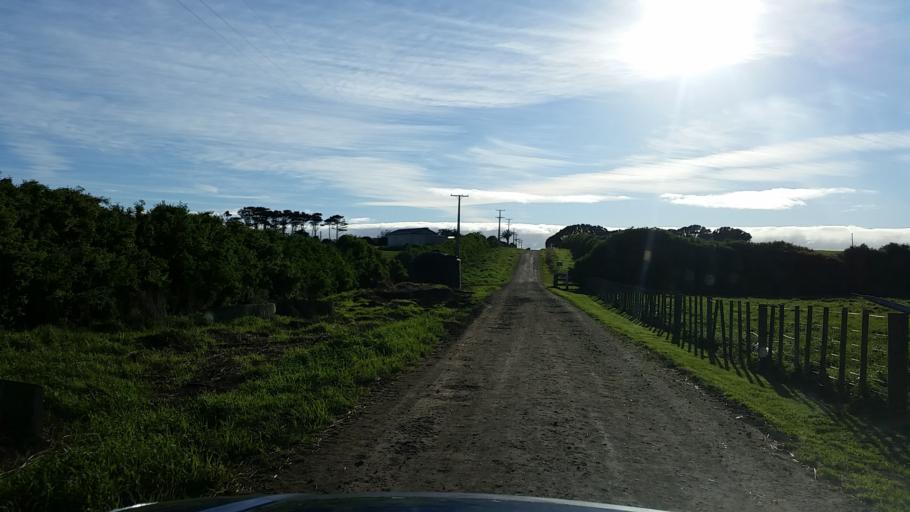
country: NZ
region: Taranaki
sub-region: South Taranaki District
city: Patea
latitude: -39.7164
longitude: 174.4269
